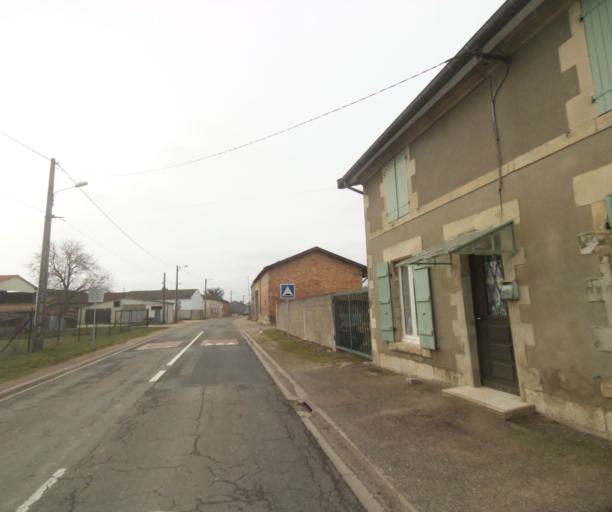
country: FR
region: Champagne-Ardenne
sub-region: Departement de la Haute-Marne
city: Villiers-en-Lieu
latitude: 48.6859
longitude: 4.8851
